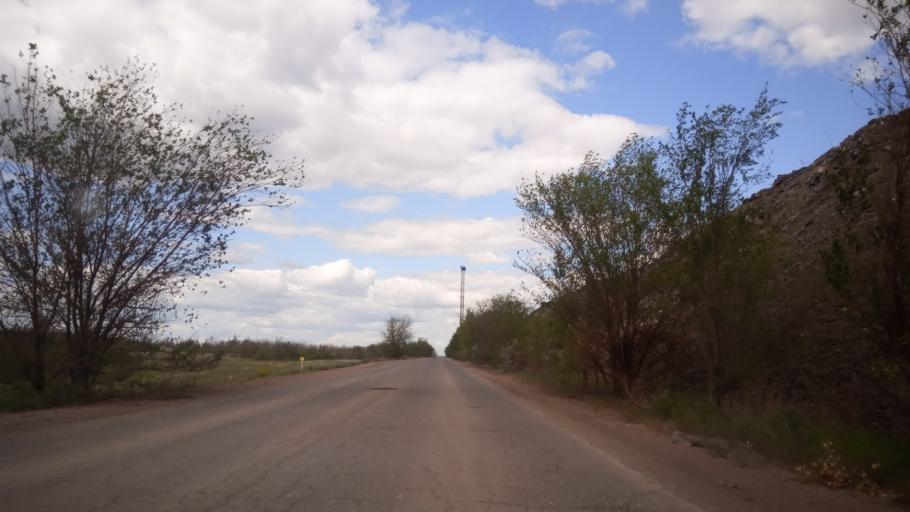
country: RU
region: Orenburg
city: Novotroitsk
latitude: 51.2473
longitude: 58.3614
